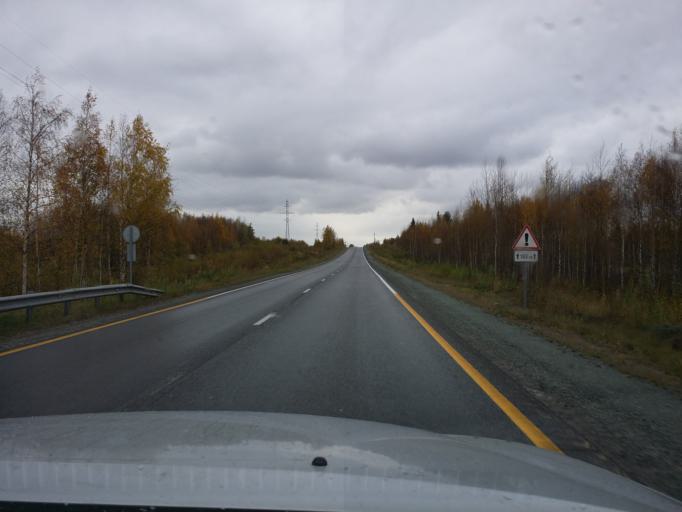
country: RU
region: Khanty-Mansiyskiy Avtonomnyy Okrug
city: Megion
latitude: 61.1022
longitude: 75.9568
